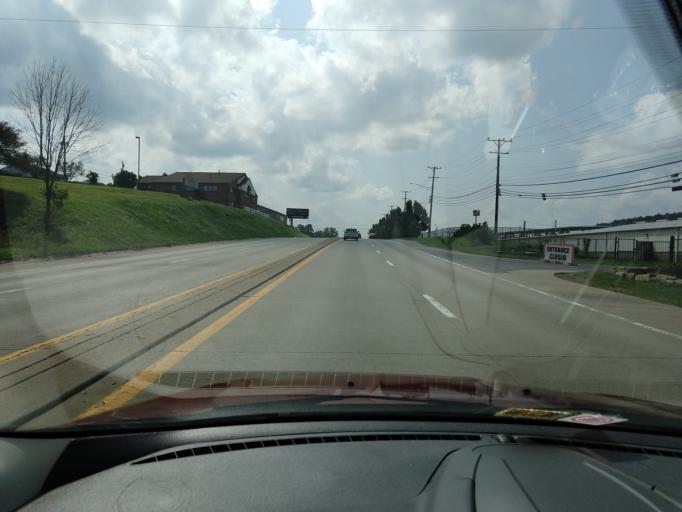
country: US
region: Pennsylvania
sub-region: Greene County
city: Morrisville
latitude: 39.8985
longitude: -80.1534
